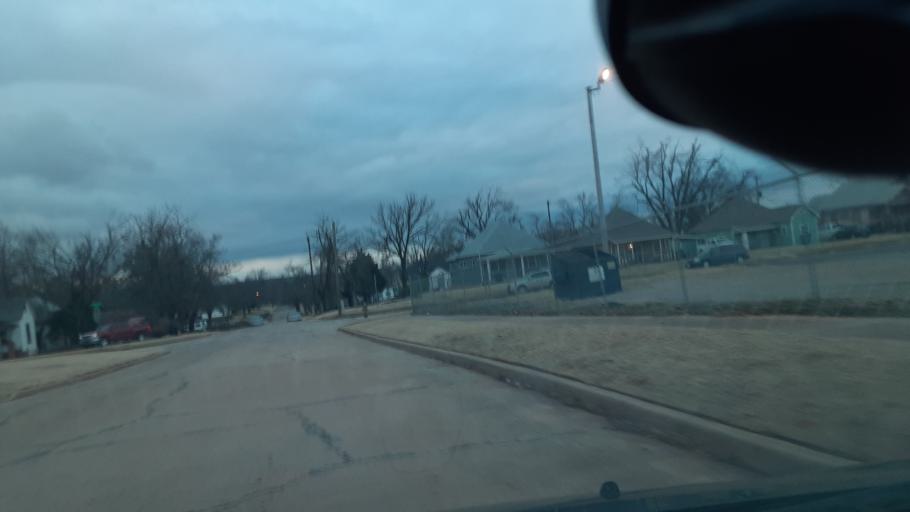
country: US
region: Oklahoma
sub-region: Logan County
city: Guthrie
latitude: 35.8765
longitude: -97.4151
